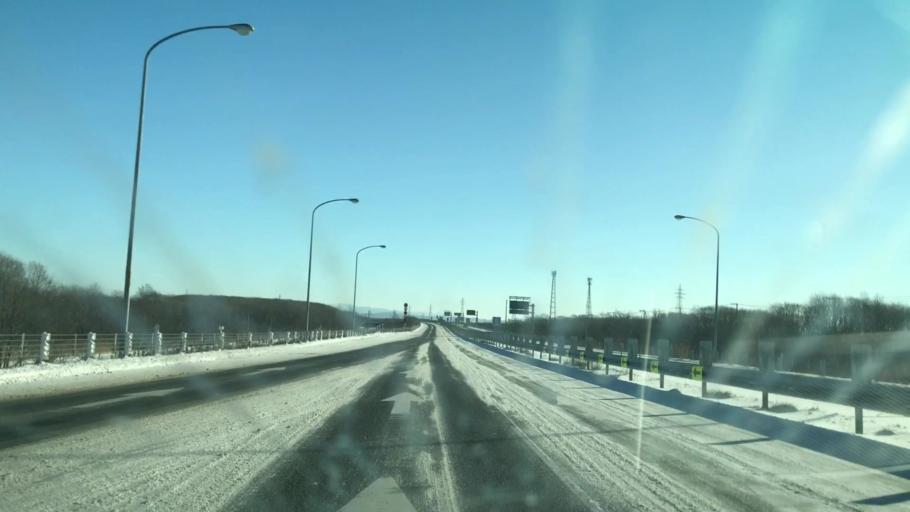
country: JP
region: Hokkaido
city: Tomakomai
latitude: 42.6745
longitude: 141.7362
